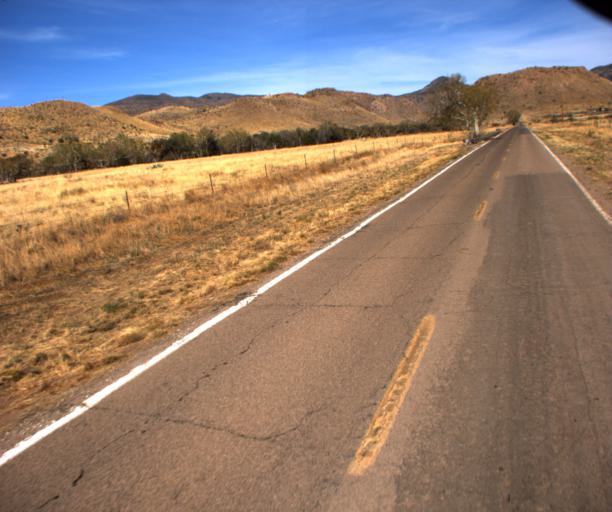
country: US
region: Arizona
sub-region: Cochise County
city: Willcox
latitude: 32.0067
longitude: -109.4047
